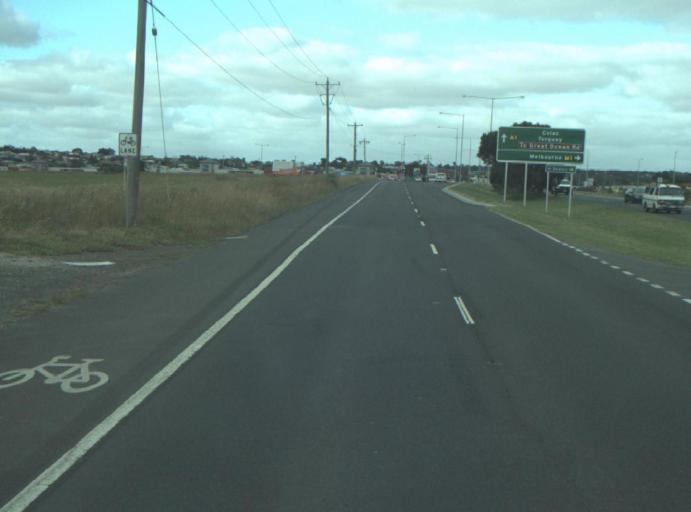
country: AU
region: Victoria
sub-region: Greater Geelong
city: Wandana Heights
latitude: -38.1991
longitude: 144.3151
